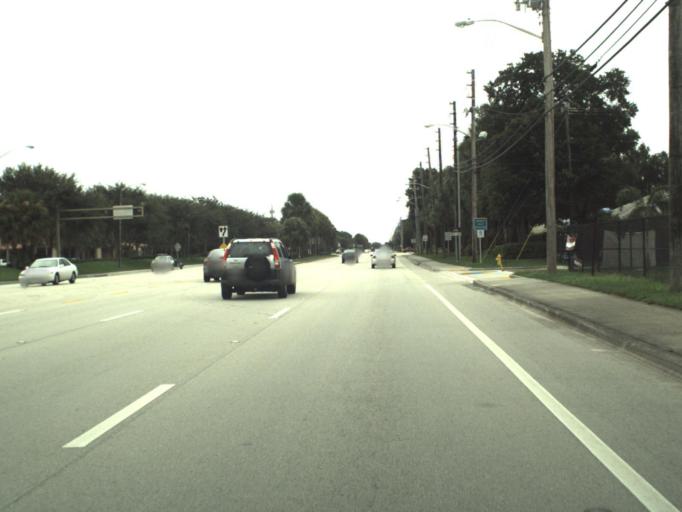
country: US
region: Florida
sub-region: Palm Beach County
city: North Palm Beach
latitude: 26.7993
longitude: -80.1065
